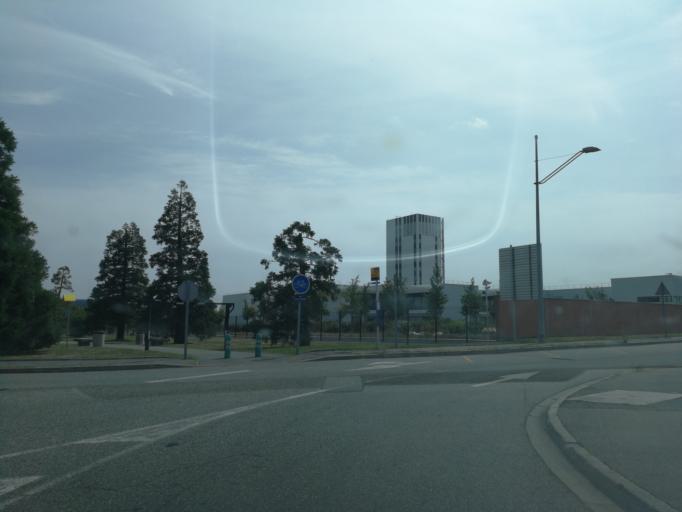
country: FR
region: Midi-Pyrenees
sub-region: Departement de la Haute-Garonne
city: Beauzelle
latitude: 43.6547
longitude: 1.3608
